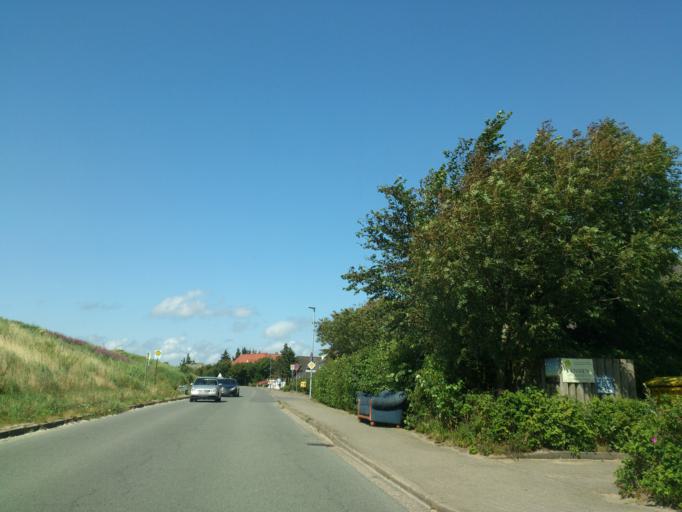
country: DE
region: Schleswig-Holstein
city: Sankt Peter-Ording
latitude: 54.3274
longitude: 8.6075
